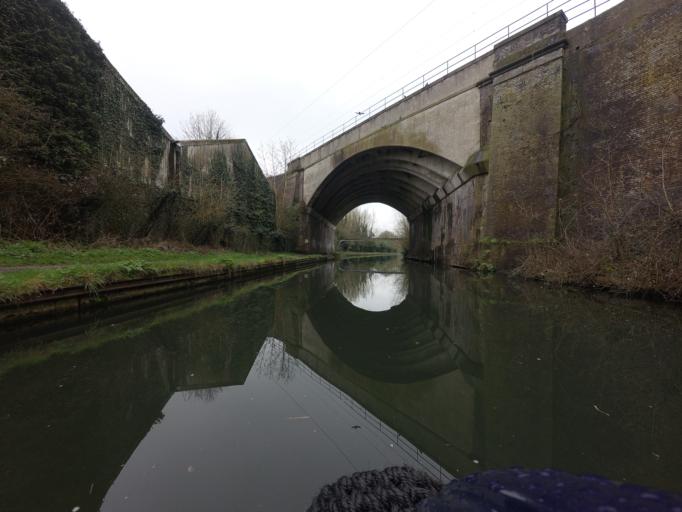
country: GB
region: England
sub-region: Hertfordshire
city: Kings Langley
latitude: 51.7249
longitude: -0.4498
